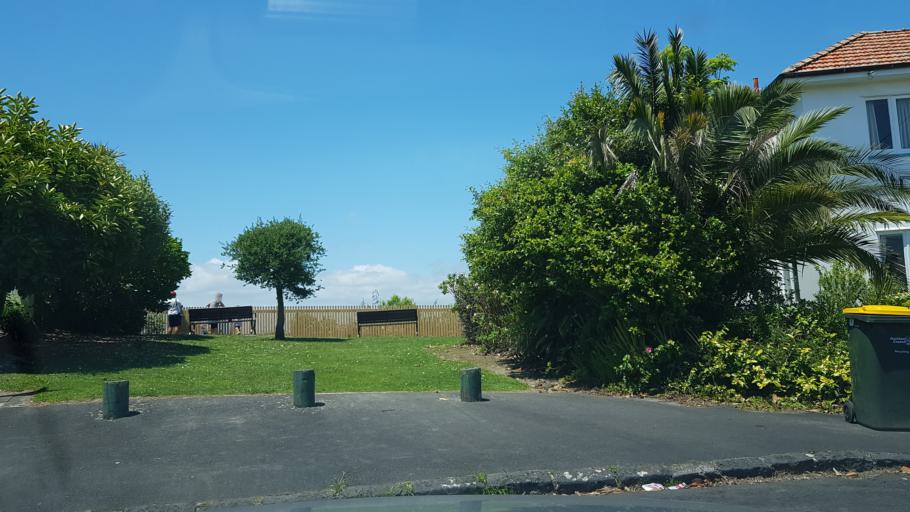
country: NZ
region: Auckland
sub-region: Auckland
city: North Shore
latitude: -36.8290
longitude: 174.7734
